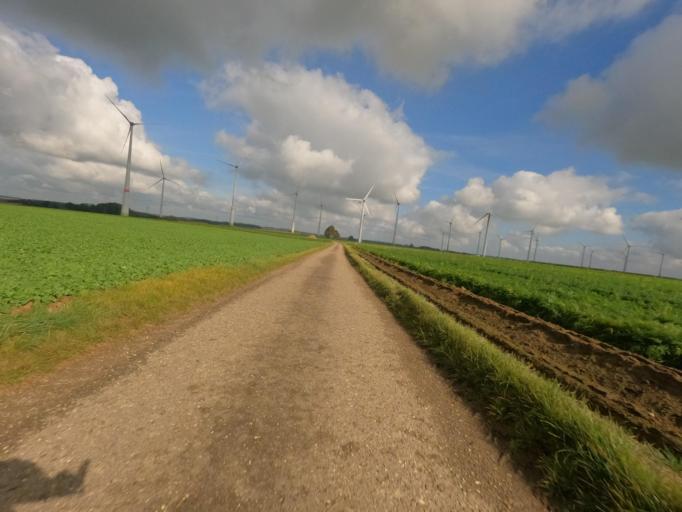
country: DE
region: North Rhine-Westphalia
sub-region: Regierungsbezirk Koln
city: Linnich
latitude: 51.0098
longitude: 6.2910
